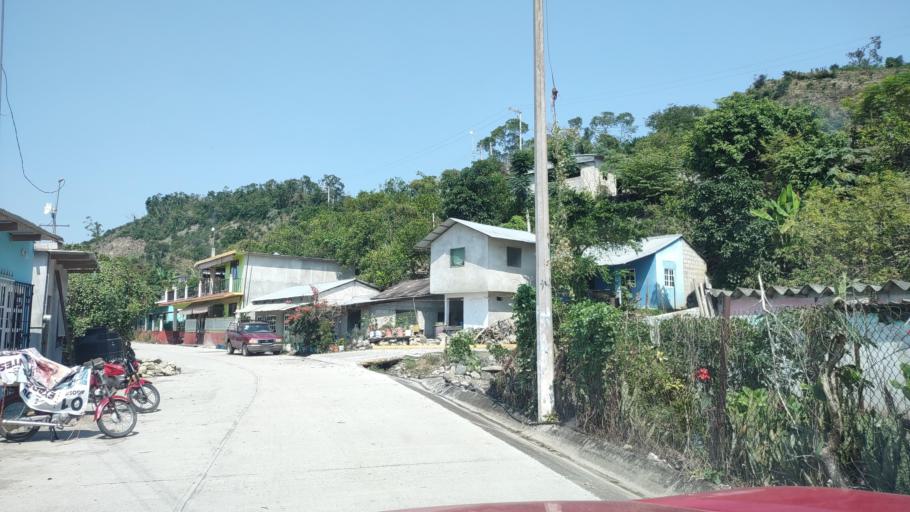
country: MX
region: Veracruz
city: Agua Dulce
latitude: 20.3102
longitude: -97.1704
